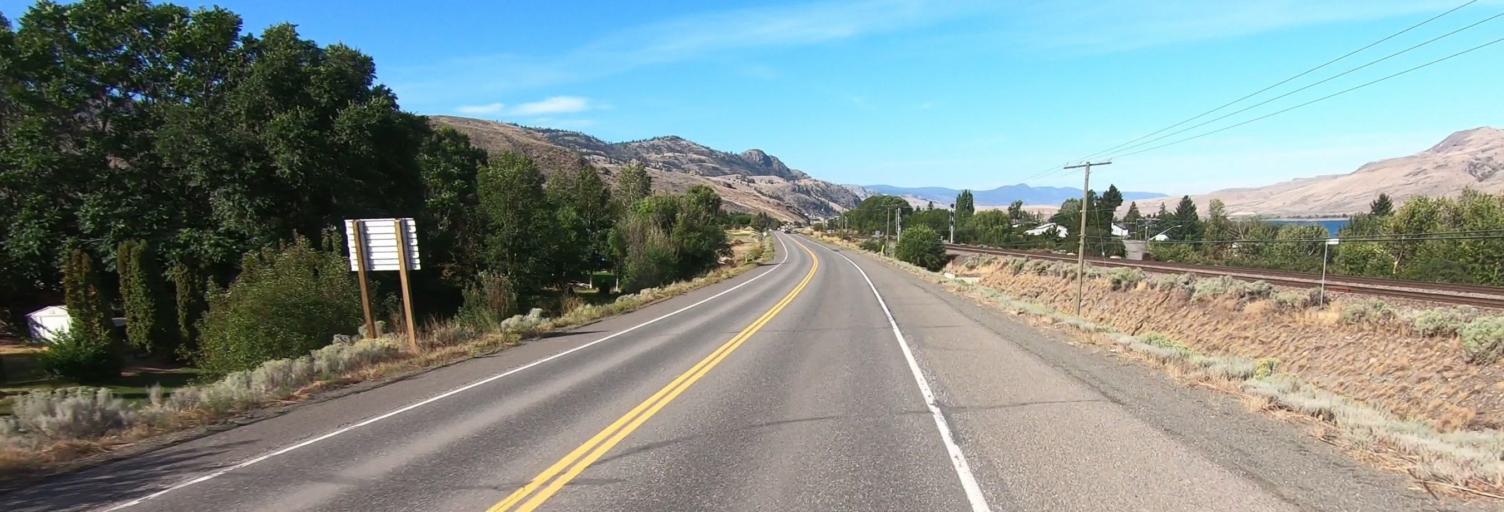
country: CA
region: British Columbia
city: Logan Lake
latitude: 50.7593
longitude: -120.8153
